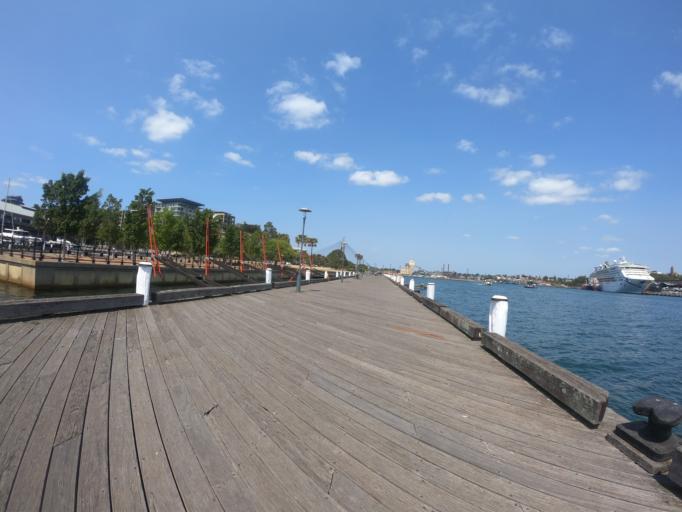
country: AU
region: New South Wales
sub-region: Leichhardt
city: Balmain East
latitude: -33.8625
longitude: 151.1939
